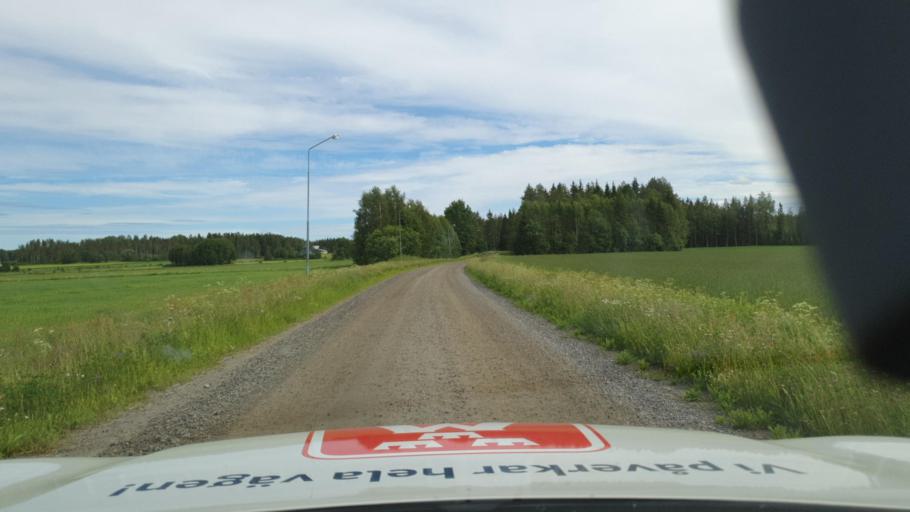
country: SE
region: Vaesterbotten
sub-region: Robertsfors Kommun
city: Robertsfors
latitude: 64.3767
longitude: 21.0354
